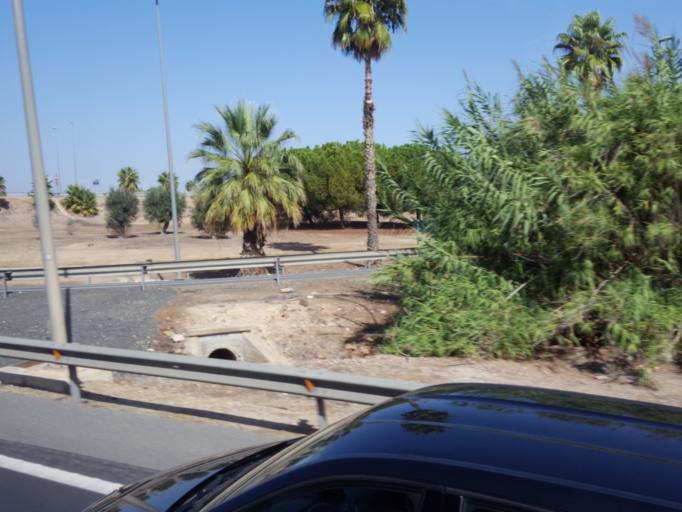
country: ES
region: Murcia
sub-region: Murcia
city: Murcia
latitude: 37.9983
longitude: -1.1518
